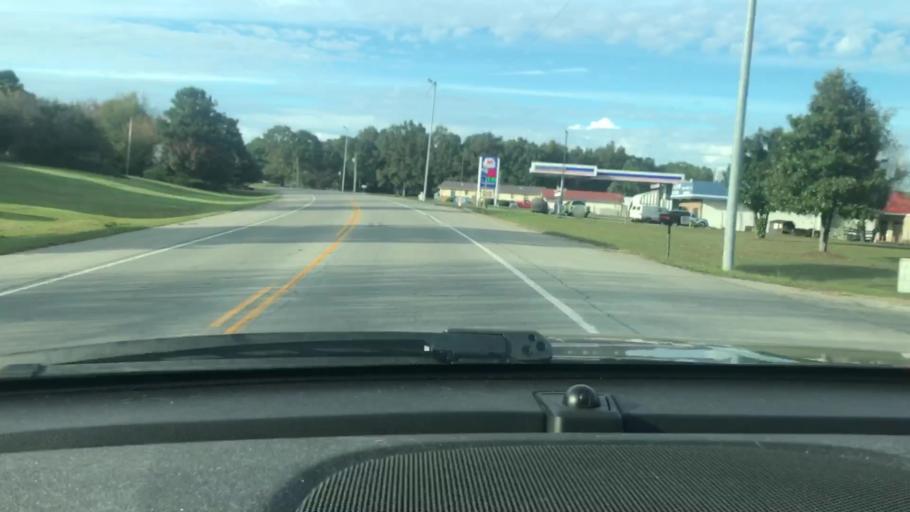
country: US
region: Tennessee
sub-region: Dickson County
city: White Bluff
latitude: 36.1254
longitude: -87.2273
